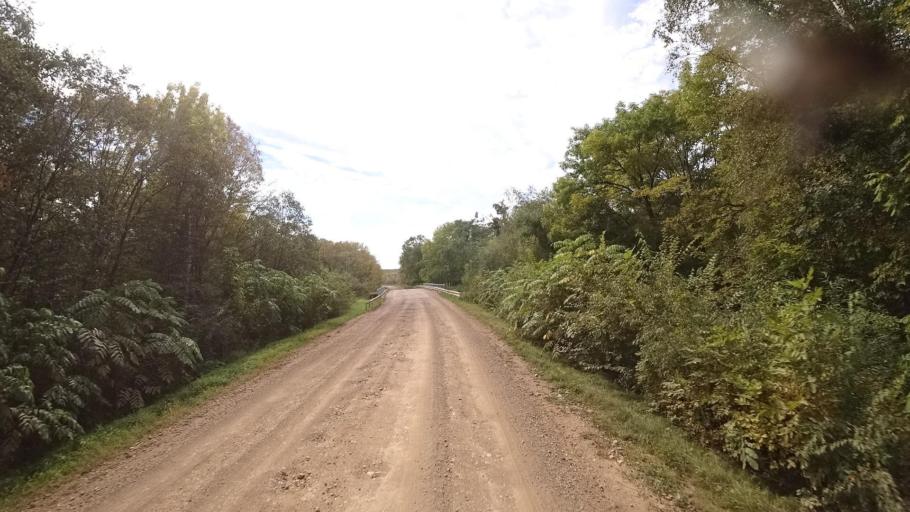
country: RU
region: Primorskiy
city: Yakovlevka
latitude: 44.5326
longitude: 133.6021
